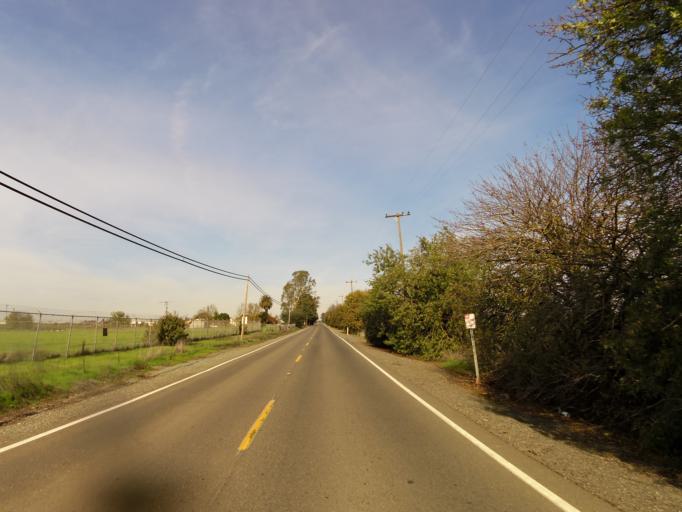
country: US
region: California
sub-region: San Joaquin County
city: Thornton
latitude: 38.3112
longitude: -121.4202
